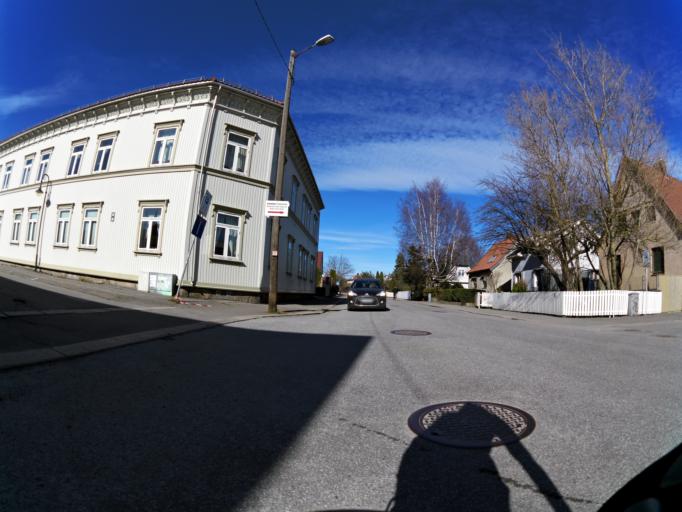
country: NO
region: Ostfold
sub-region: Fredrikstad
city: Fredrikstad
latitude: 59.2170
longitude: 10.9303
